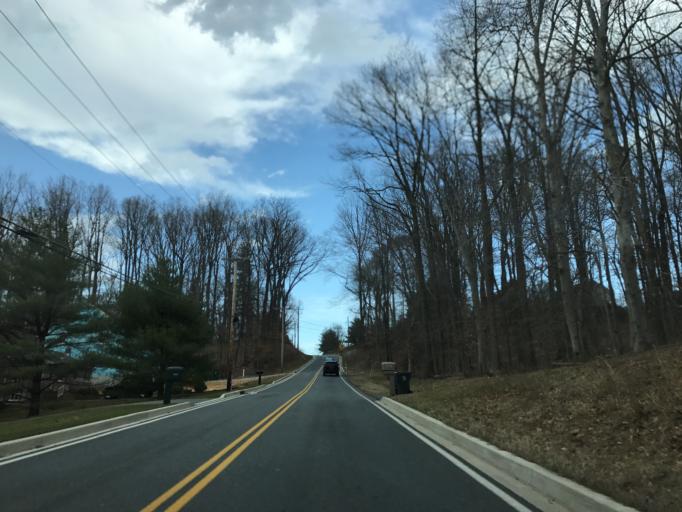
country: US
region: Maryland
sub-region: Harford County
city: Bel Air South
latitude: 39.5080
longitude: -76.3020
